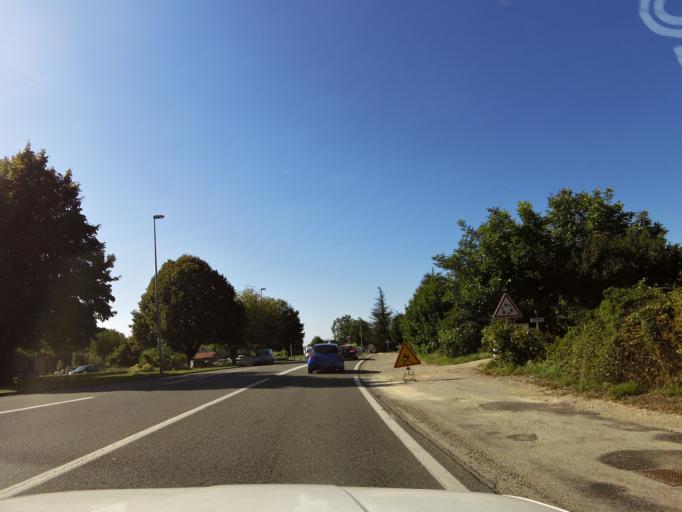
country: FR
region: Rhone-Alpes
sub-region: Departement de l'Ain
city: Vaux-en-Bugey
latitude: 45.9468
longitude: 5.3690
